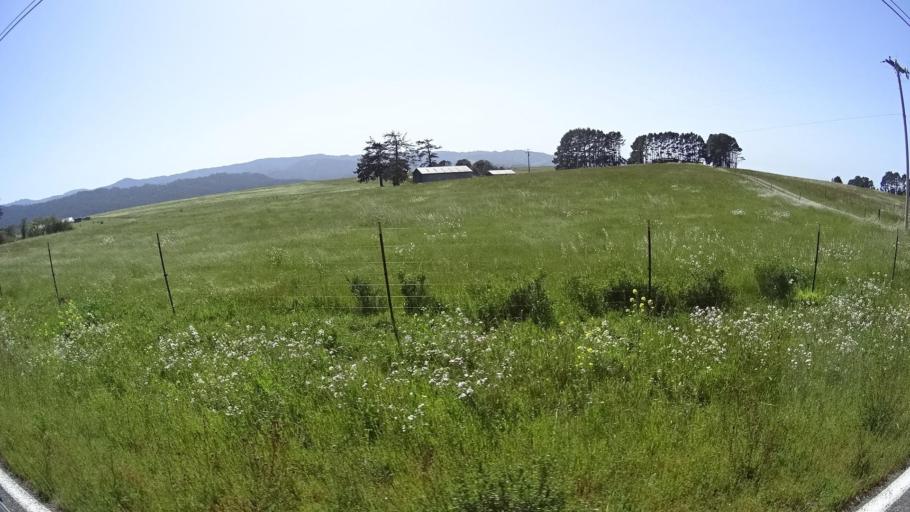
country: US
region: California
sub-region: Humboldt County
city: Hydesville
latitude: 40.5540
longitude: -124.1210
